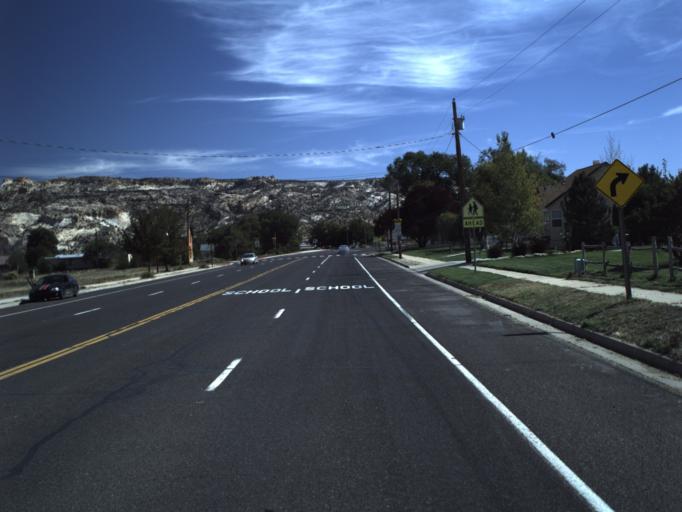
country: US
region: Utah
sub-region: Wayne County
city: Loa
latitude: 37.7702
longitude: -111.5981
